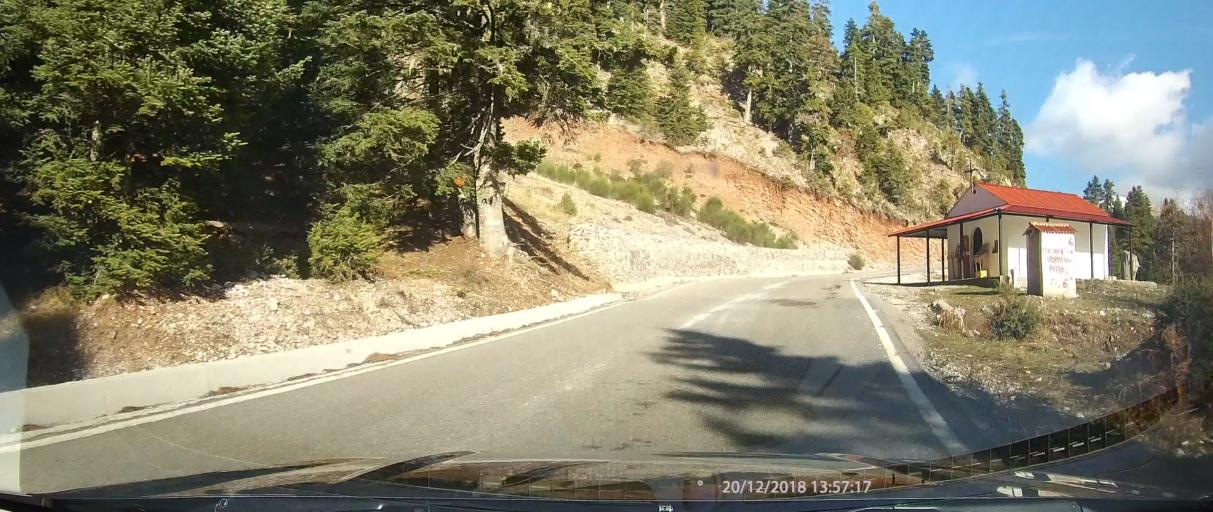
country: GR
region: West Greece
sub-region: Nomos Aitolias kai Akarnanias
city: Thermo
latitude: 38.7094
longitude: 21.6203
